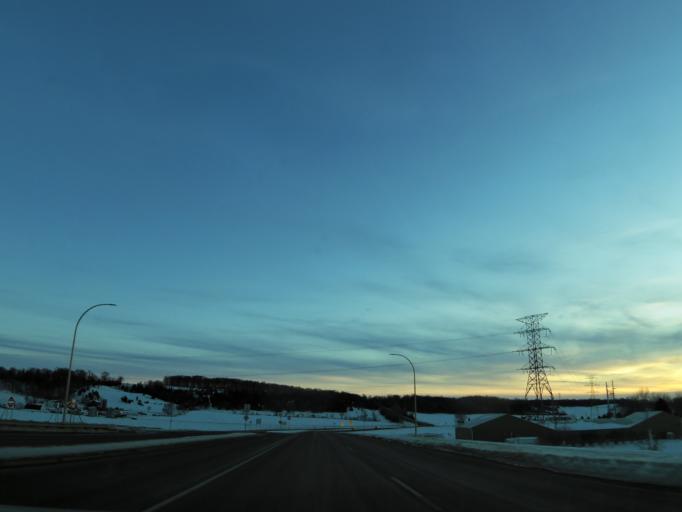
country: US
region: Minnesota
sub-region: Scott County
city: Shakopee
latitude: 44.7774
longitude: -93.5598
